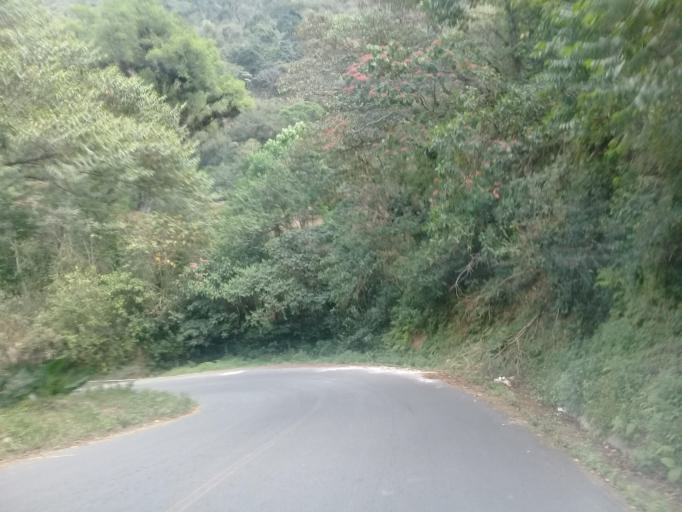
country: MX
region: Veracruz
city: Jalapilla
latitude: 18.8140
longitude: -97.0612
